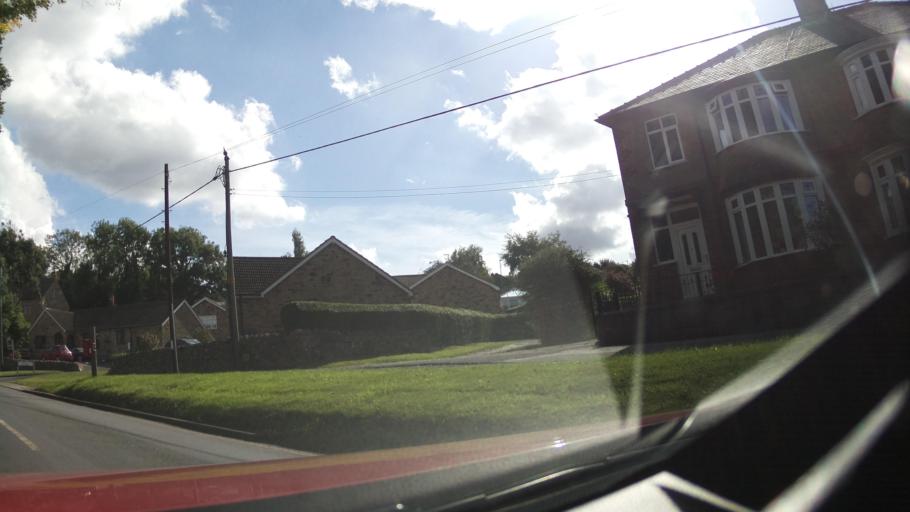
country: GB
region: England
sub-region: North Yorkshire
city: Leyburn
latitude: 54.2887
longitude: -1.8089
